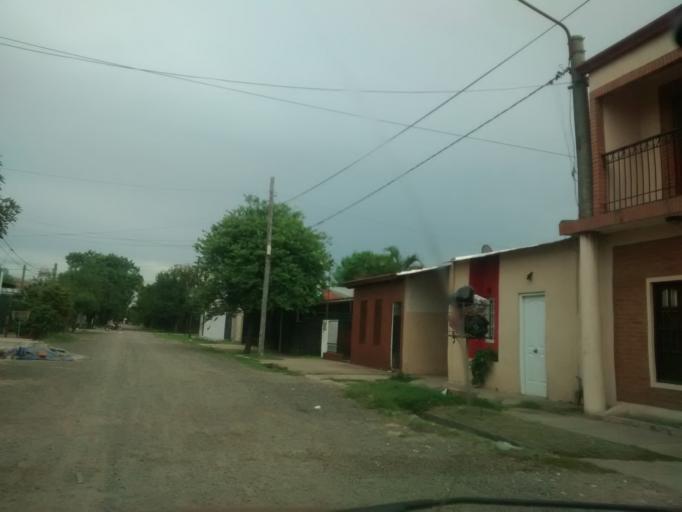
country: AR
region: Chaco
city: Fontana
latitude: -27.4501
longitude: -59.0222
